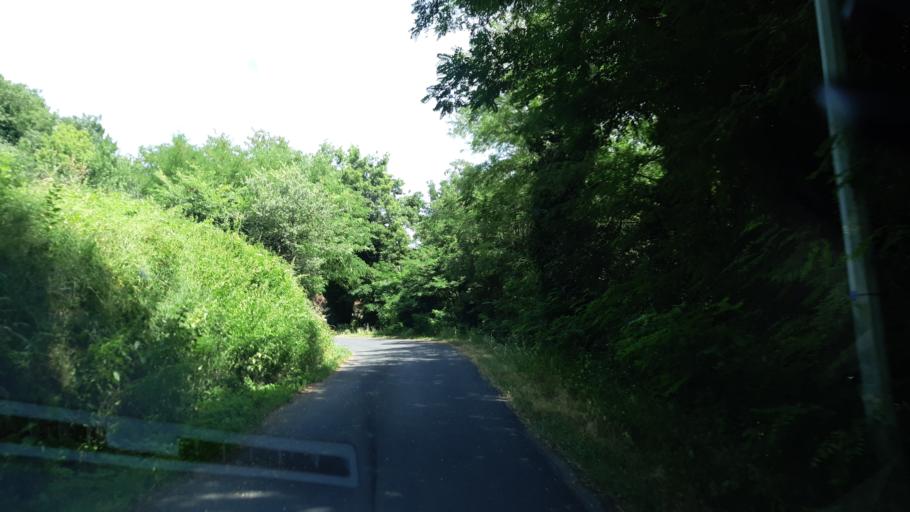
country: FR
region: Languedoc-Roussillon
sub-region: Departement des Pyrenees-Orientales
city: Arles
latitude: 42.5373
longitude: 2.5865
